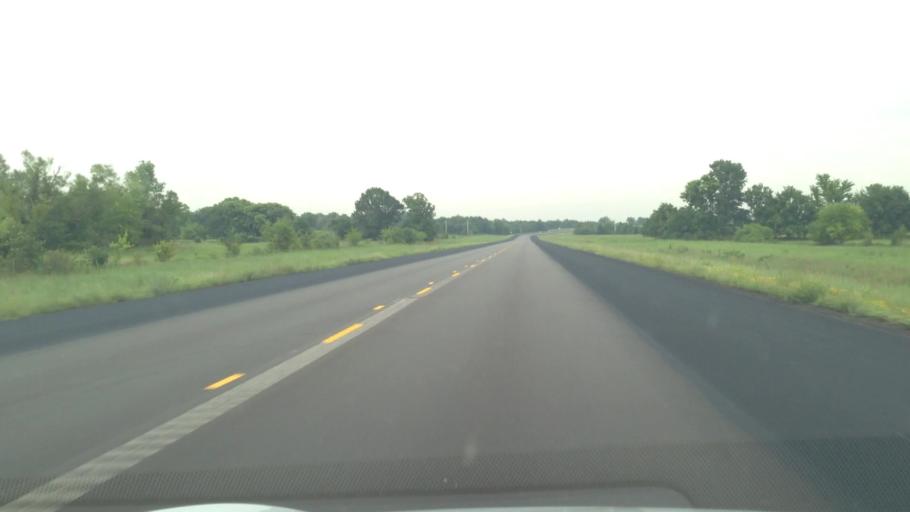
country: US
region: Kansas
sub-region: Cherokee County
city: Baxter Springs
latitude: 37.0332
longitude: -94.7058
